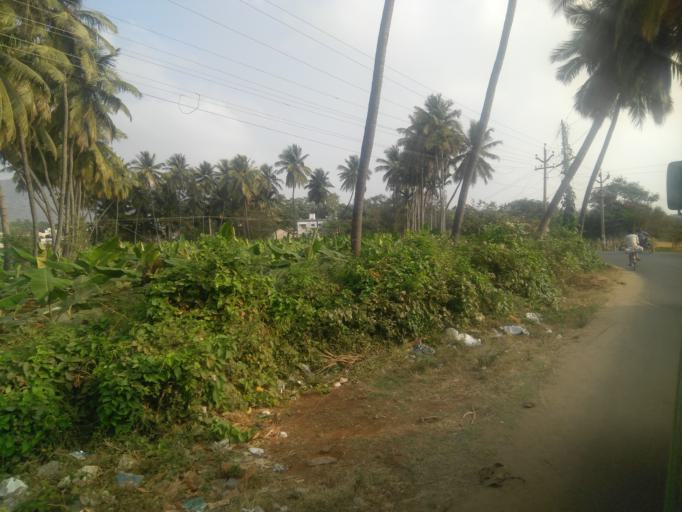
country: IN
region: Tamil Nadu
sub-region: Coimbatore
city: Perur
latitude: 11.0438
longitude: 76.8946
